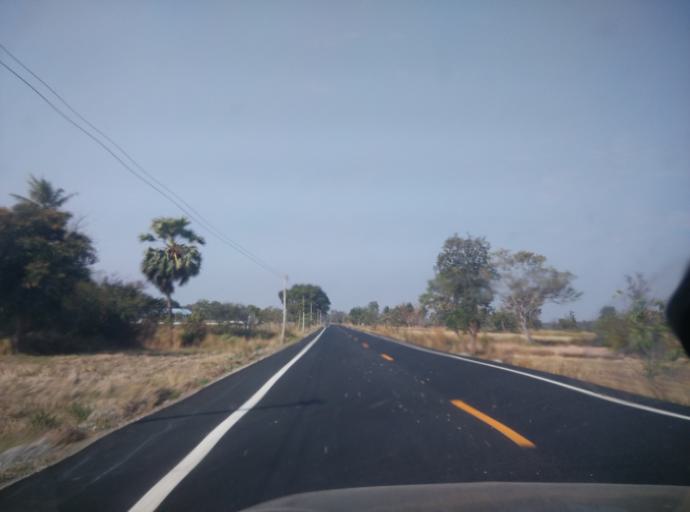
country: TH
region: Sisaket
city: Si Sa Ket
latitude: 15.1234
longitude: 104.2433
